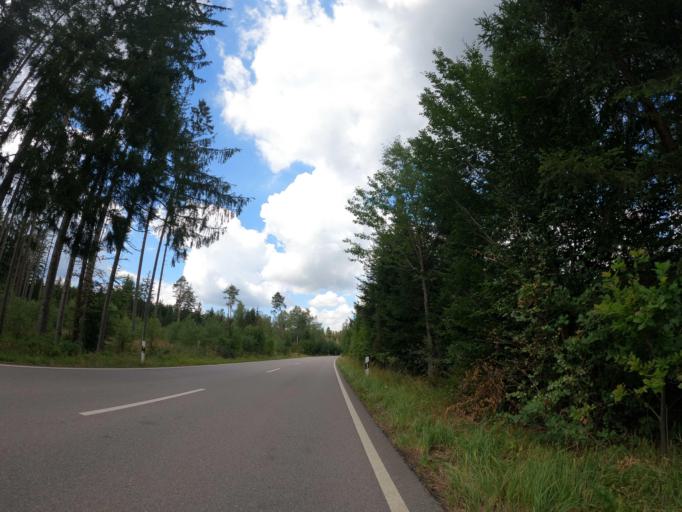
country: DE
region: Bavaria
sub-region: Upper Bavaria
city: Ottobrunn
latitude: 48.0413
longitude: 11.6714
